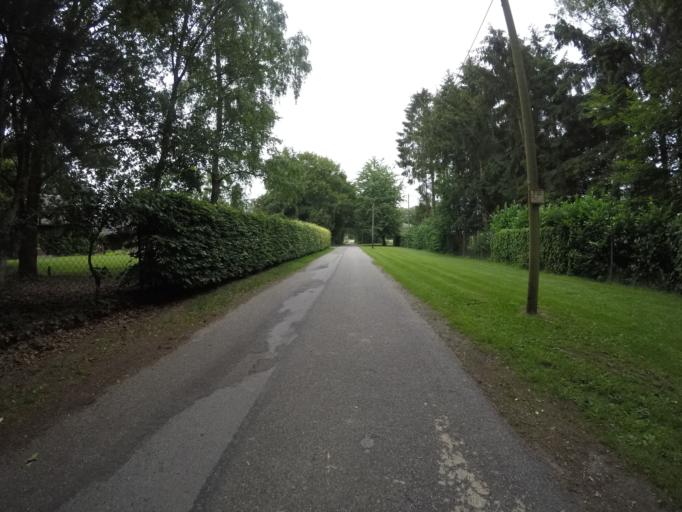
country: NL
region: Gelderland
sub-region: Oude IJsselstreek
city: Gendringen
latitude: 51.8548
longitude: 6.4153
